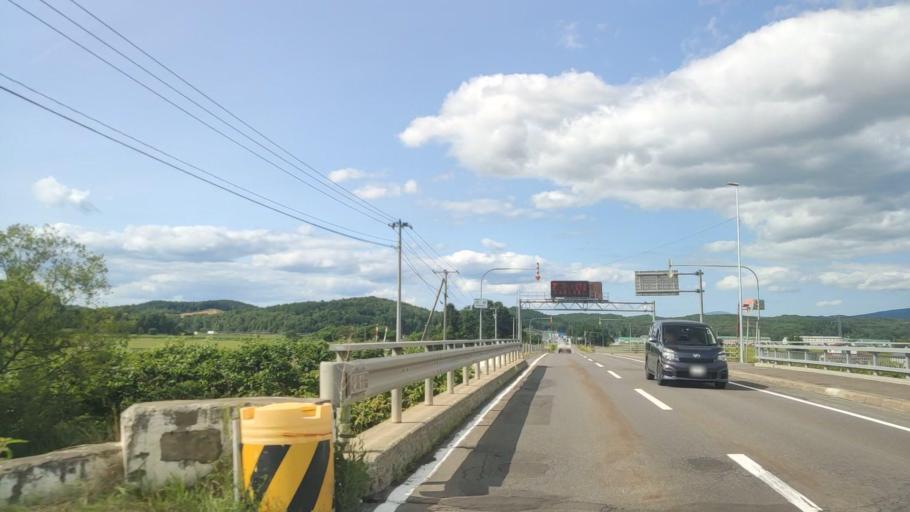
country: JP
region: Hokkaido
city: Nayoro
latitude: 44.3721
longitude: 142.4361
